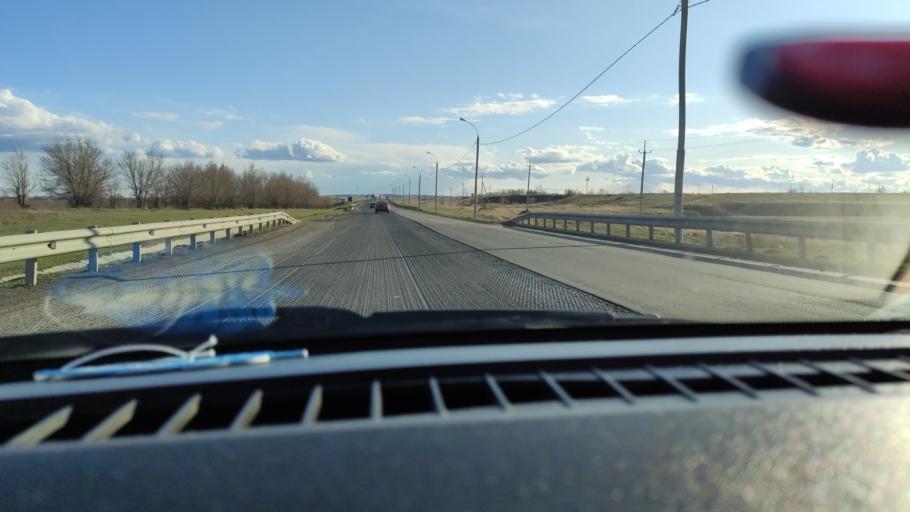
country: RU
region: Saratov
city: Yelshanka
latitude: 51.8176
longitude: 46.2124
